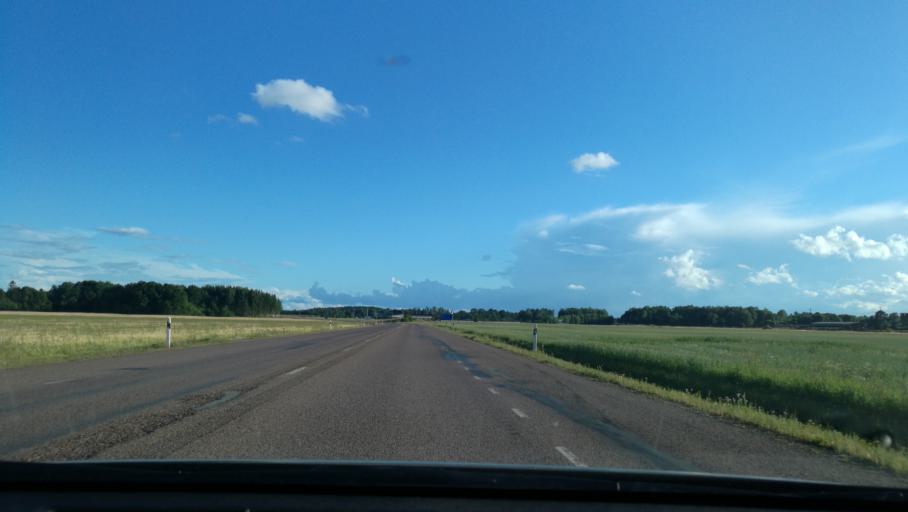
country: SE
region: Vaestmanland
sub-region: Kopings Kommun
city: Koping
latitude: 59.4878
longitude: 15.9863
